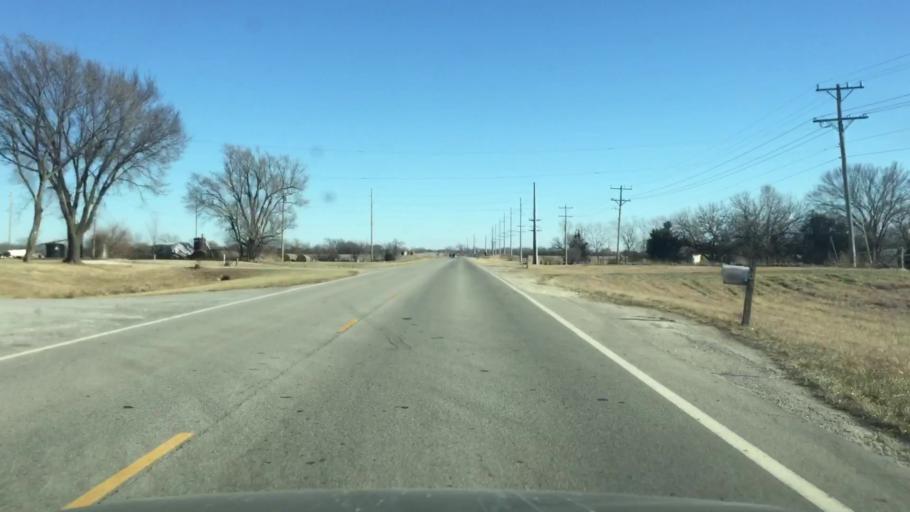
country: US
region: Kansas
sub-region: Allen County
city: Humboldt
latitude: 37.8201
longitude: -95.4222
